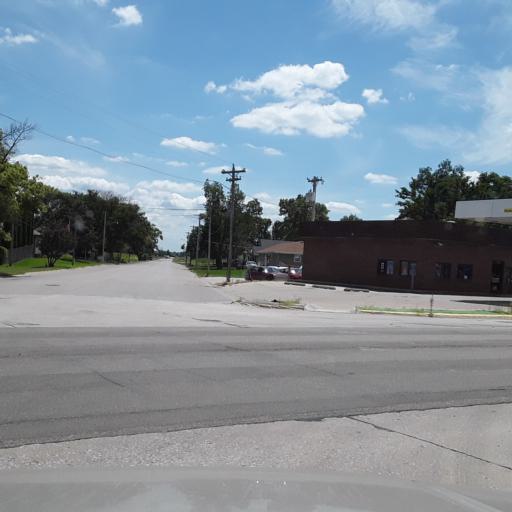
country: US
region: Nebraska
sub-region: Platte County
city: Columbus
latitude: 41.3885
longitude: -97.4933
